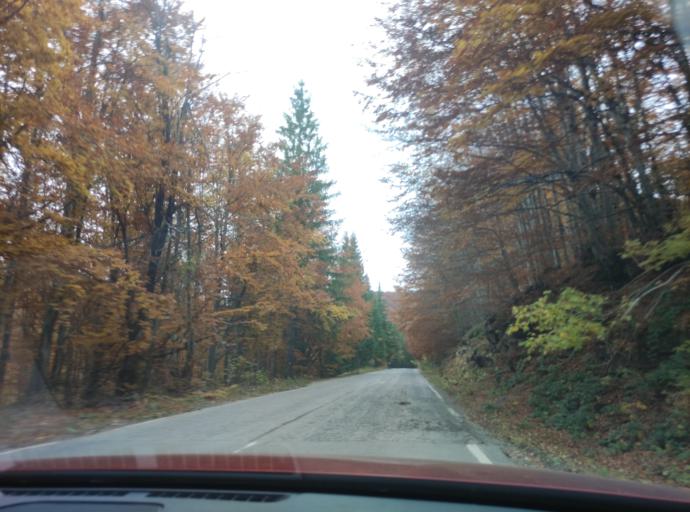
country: BG
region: Sofiya
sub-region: Obshtina Godech
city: Godech
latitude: 43.1111
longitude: 23.1122
